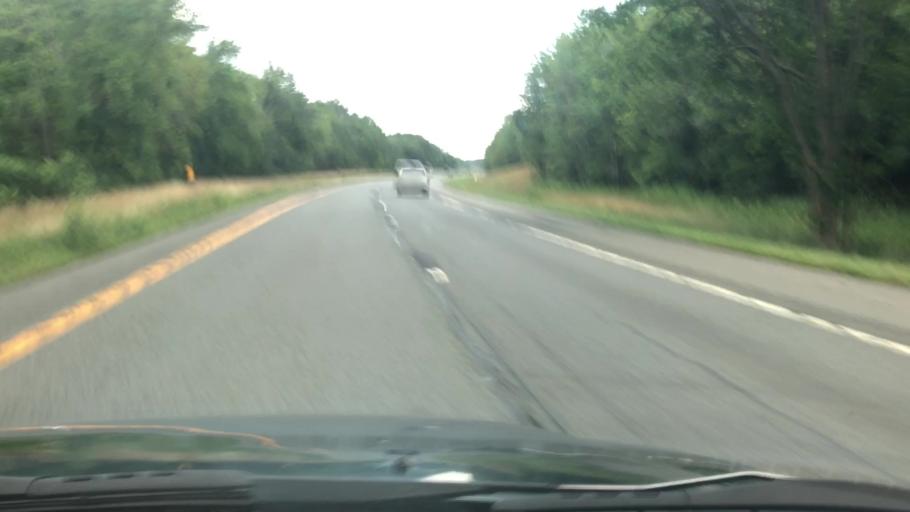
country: US
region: New York
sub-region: Orange County
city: Otisville
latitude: 41.3894
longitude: -74.5673
